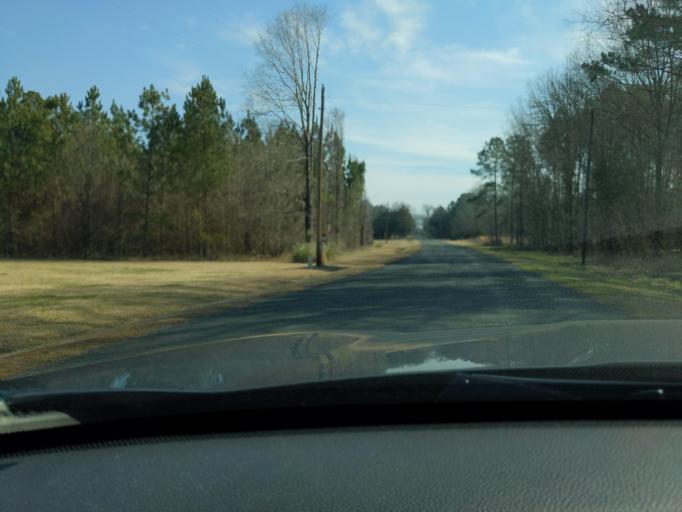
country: US
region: South Carolina
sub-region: Abbeville County
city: Calhoun Falls
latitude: 34.0931
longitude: -82.5606
